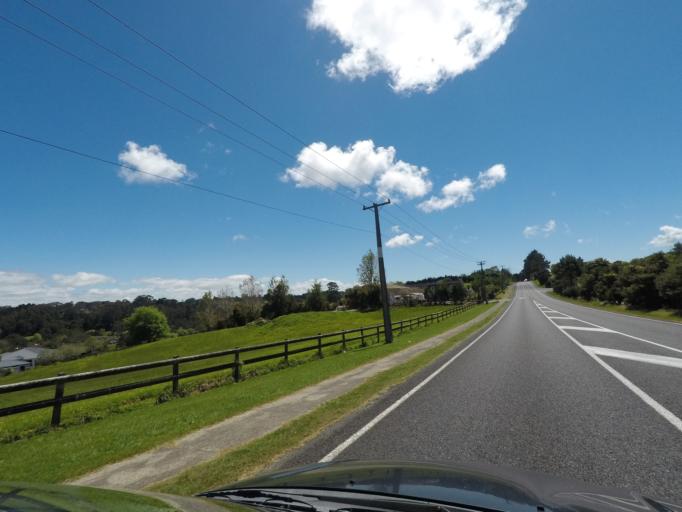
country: NZ
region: Auckland
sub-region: Auckland
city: Rothesay Bay
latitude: -36.7496
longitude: 174.6700
